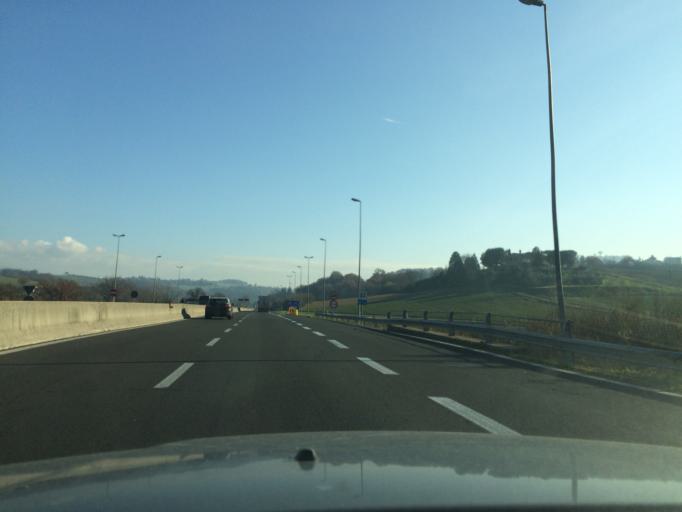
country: IT
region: Umbria
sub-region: Provincia di Perugia
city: Todi
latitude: 42.7874
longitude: 12.4287
